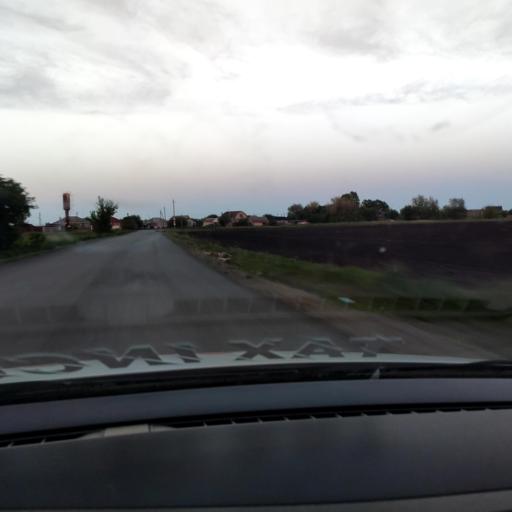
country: RU
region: Voronezj
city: Novovoronezh
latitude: 51.4128
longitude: 39.3024
